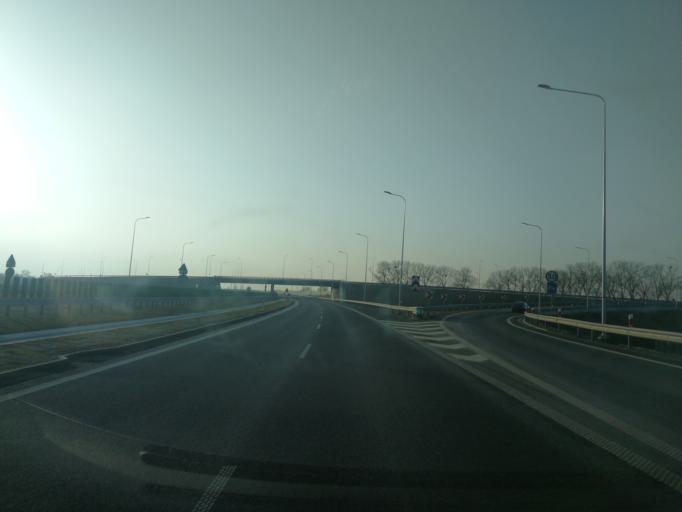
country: PL
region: Warmian-Masurian Voivodeship
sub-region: Powiat elblaski
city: Elblag
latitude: 54.1637
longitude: 19.3489
